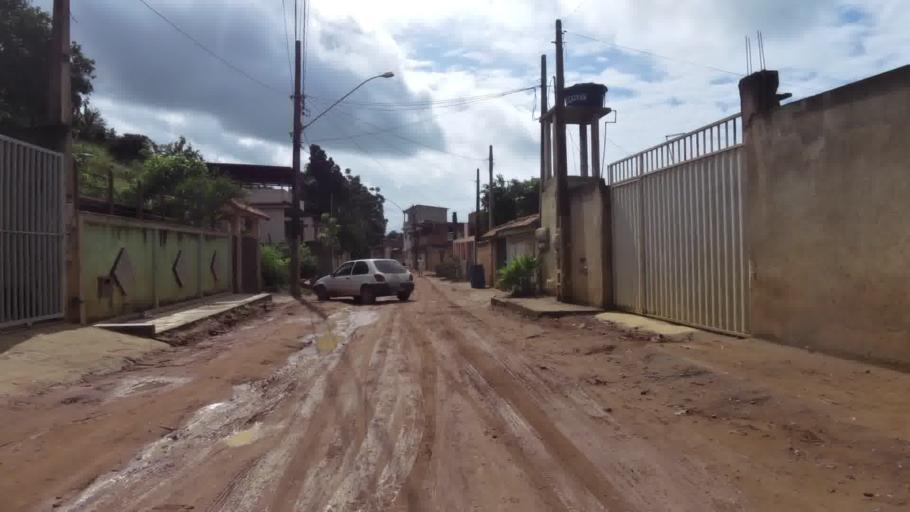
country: BR
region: Espirito Santo
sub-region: Marataizes
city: Marataizes
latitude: -21.0305
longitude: -40.8205
